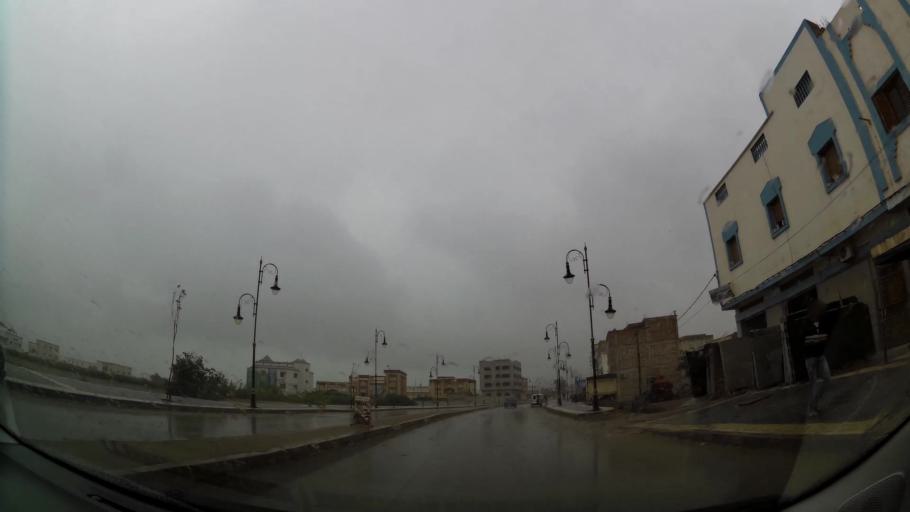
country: MA
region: Taza-Al Hoceima-Taounate
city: Imzourene
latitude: 35.1184
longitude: -3.8423
